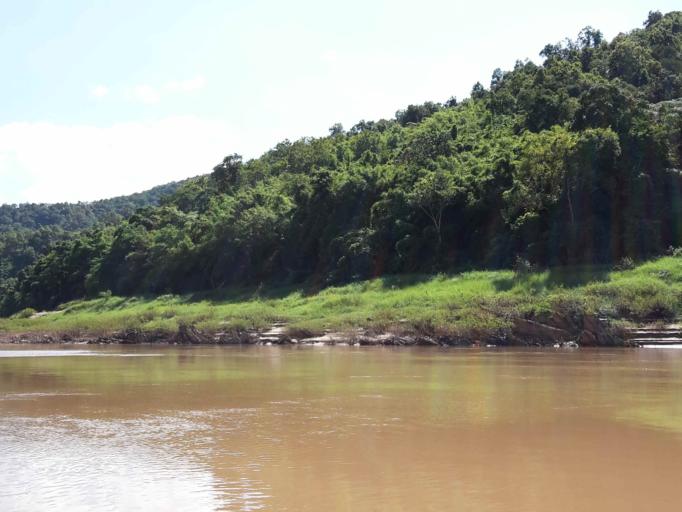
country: TH
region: Nan
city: Chaloem Phra Kiat
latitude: 19.8317
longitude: 101.4451
